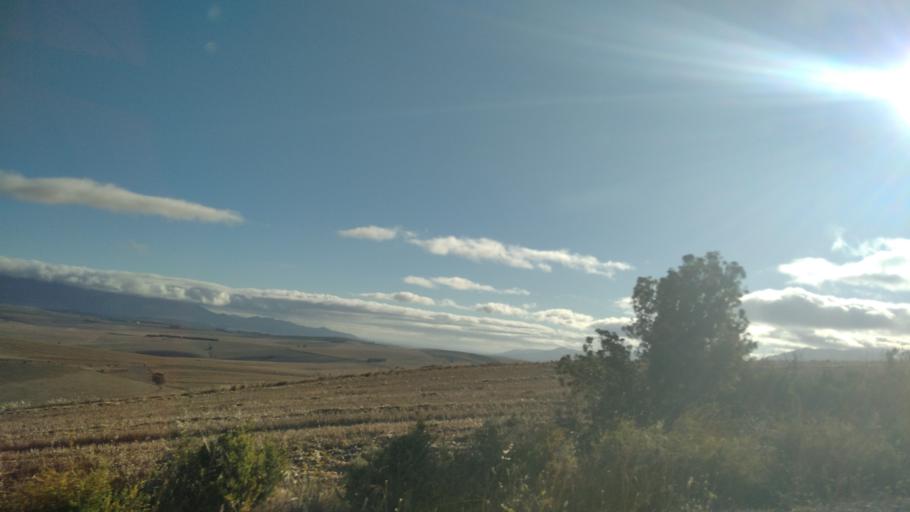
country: ZA
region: Western Cape
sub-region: Overberg District Municipality
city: Caledon
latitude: -34.1545
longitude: 19.3021
